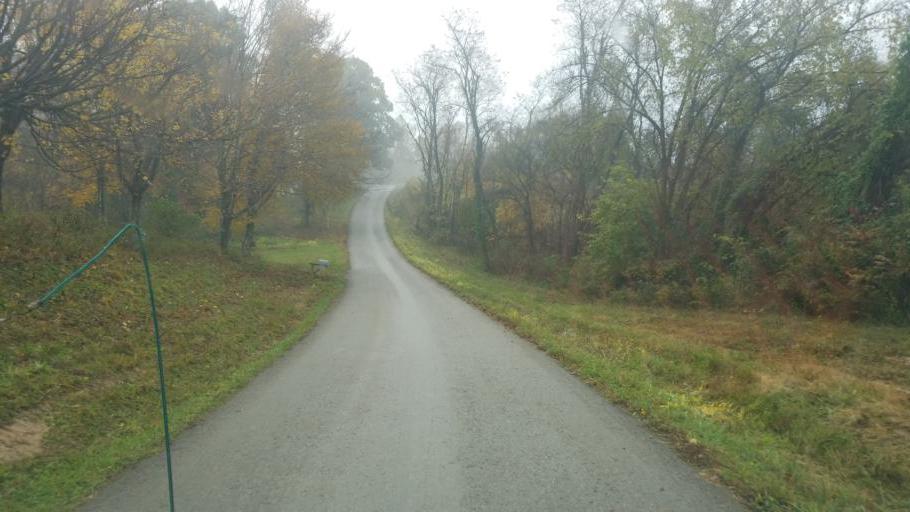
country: US
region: Ohio
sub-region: Morgan County
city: McConnelsville
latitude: 39.4973
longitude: -81.8167
